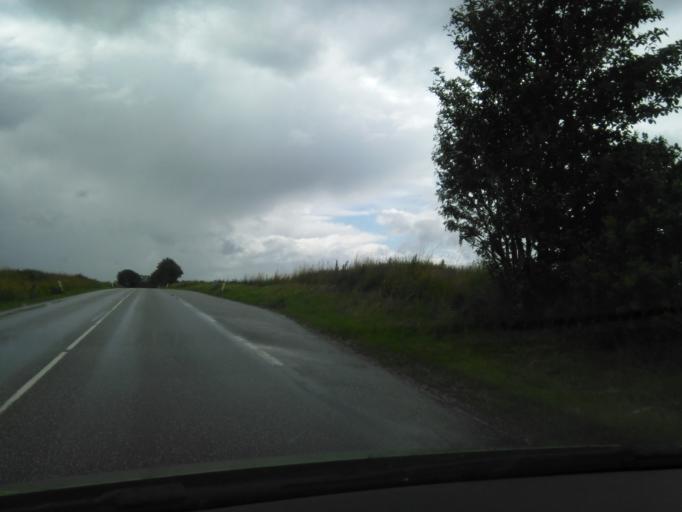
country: DK
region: Central Jutland
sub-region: Skanderborg Kommune
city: Ry
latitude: 56.0203
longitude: 9.8164
